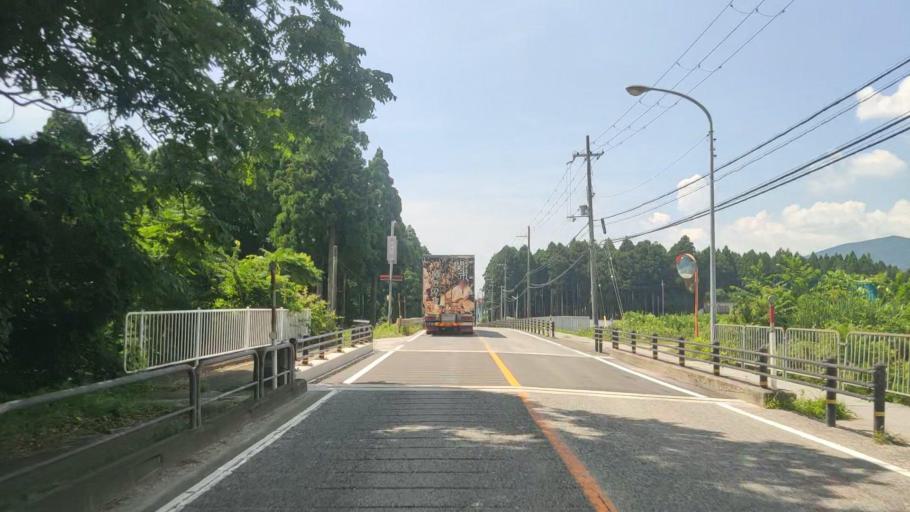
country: JP
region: Shiga Prefecture
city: Nagahama
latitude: 35.3752
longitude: 136.3839
